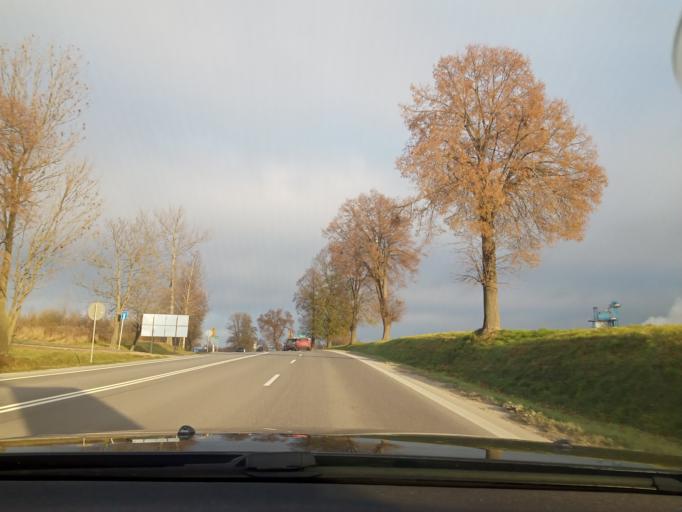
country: PL
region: Lesser Poland Voivodeship
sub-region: Powiat miechowski
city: Miechow
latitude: 50.3211
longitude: 20.0359
